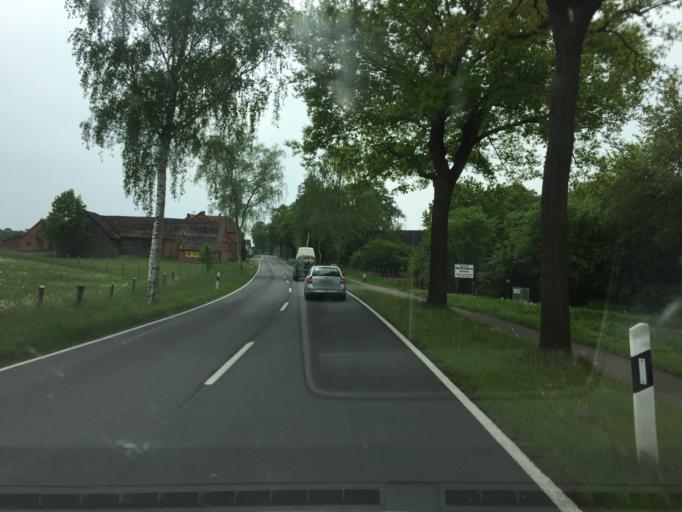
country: DE
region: Lower Saxony
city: Syke
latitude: 52.8833
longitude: 8.7806
